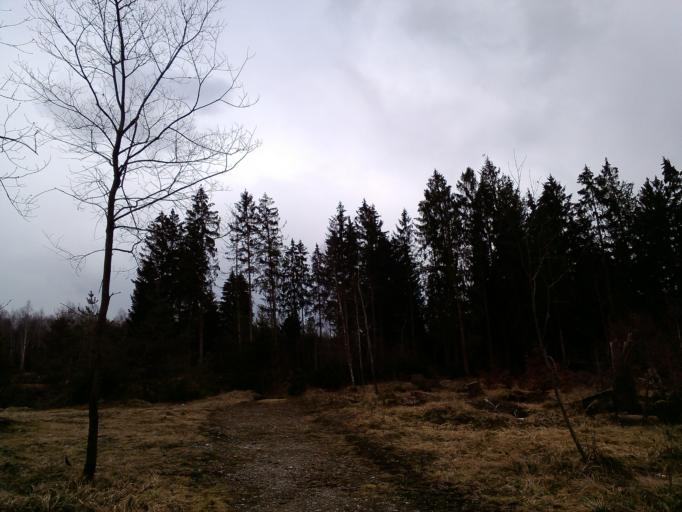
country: DE
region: Bavaria
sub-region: Upper Bavaria
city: Gauting
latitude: 48.0958
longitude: 11.3545
